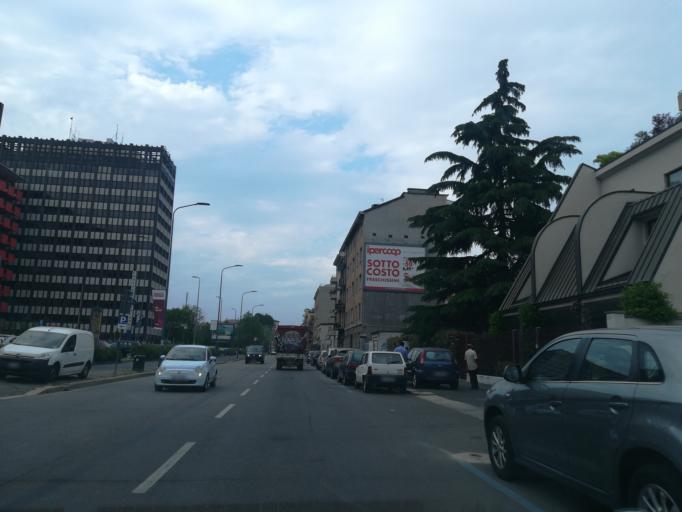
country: IT
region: Lombardy
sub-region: Citta metropolitana di Milano
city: Milano
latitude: 45.4980
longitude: 9.1915
